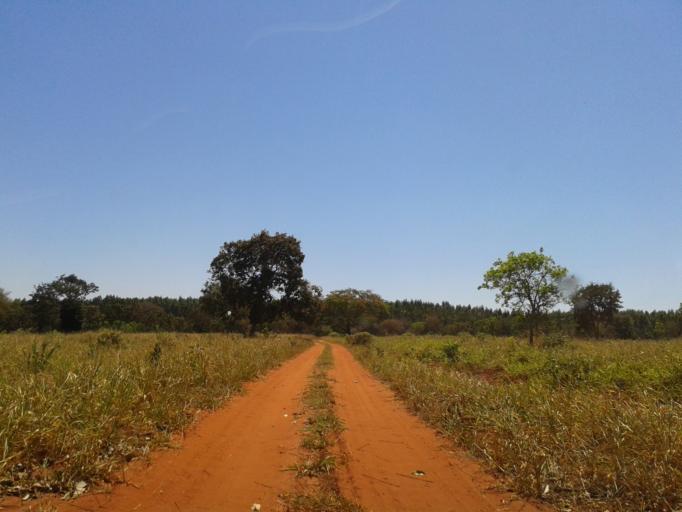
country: BR
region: Minas Gerais
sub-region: Ituiutaba
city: Ituiutaba
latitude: -19.0939
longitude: -49.2564
